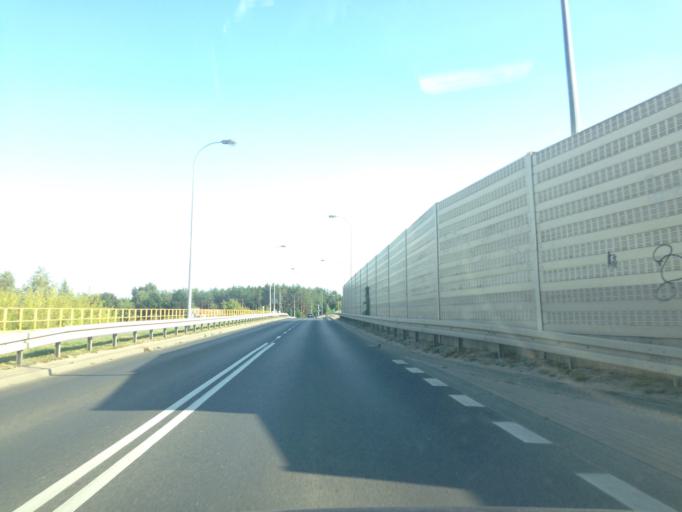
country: PL
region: Warmian-Masurian Voivodeship
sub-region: Powiat ilawski
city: Ilawa
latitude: 53.5936
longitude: 19.5835
